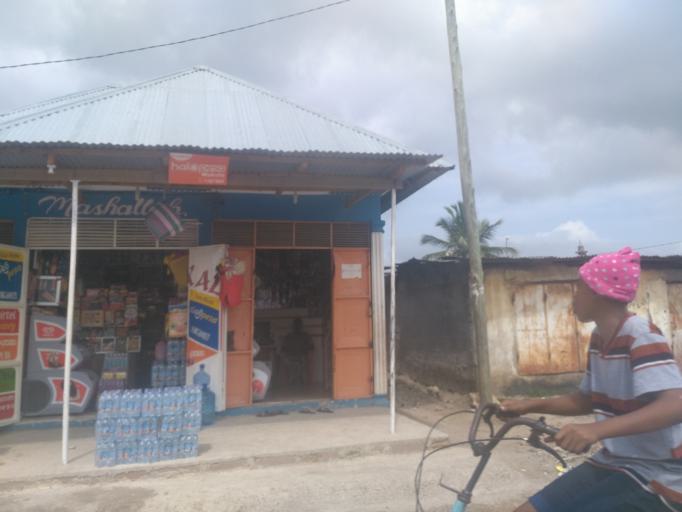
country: TZ
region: Zanzibar Urban/West
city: Zanzibar
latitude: -6.1776
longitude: 39.2396
